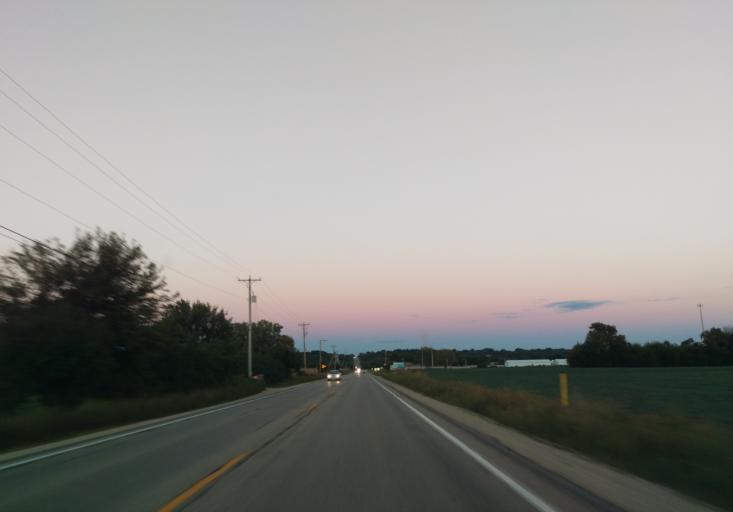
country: US
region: Wisconsin
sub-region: Rock County
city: Janesville
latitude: 42.7302
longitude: -89.0722
